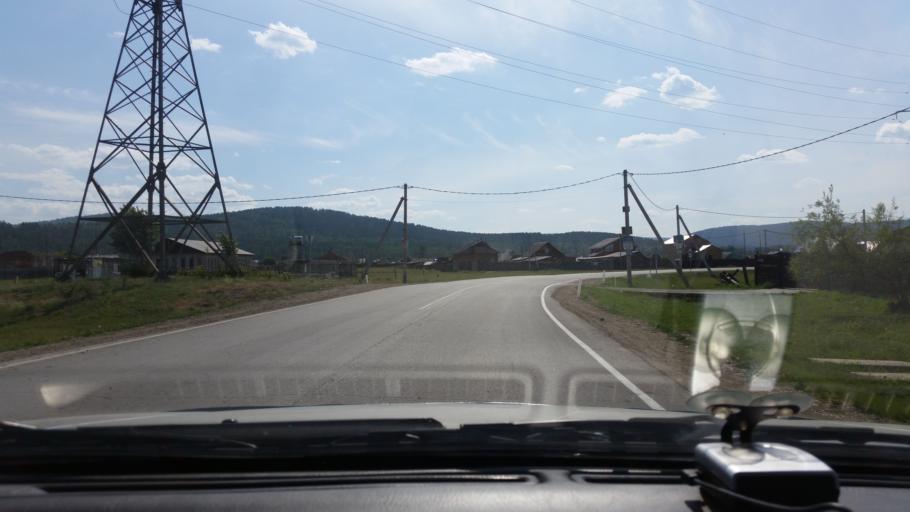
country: RU
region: Irkutsk
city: Baklashi
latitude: 52.2040
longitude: 103.9557
